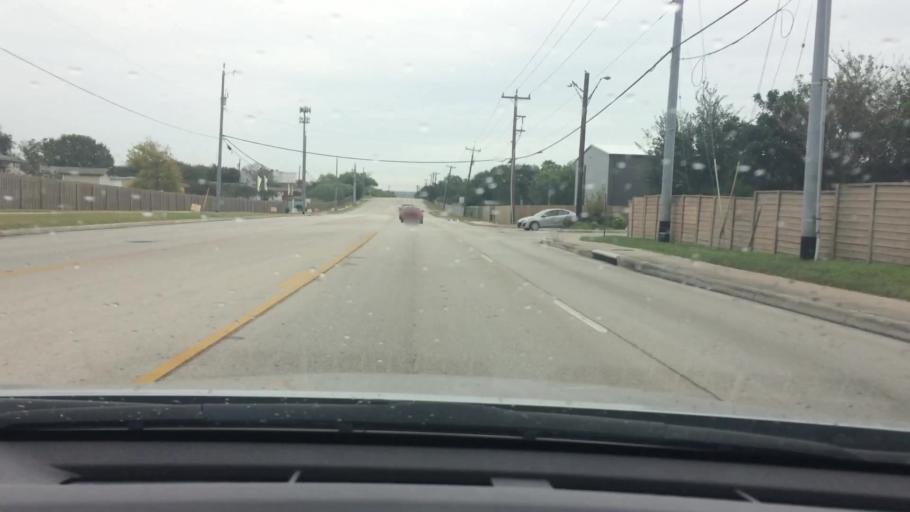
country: US
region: Texas
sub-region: Bexar County
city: Converse
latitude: 29.5209
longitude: -98.3421
